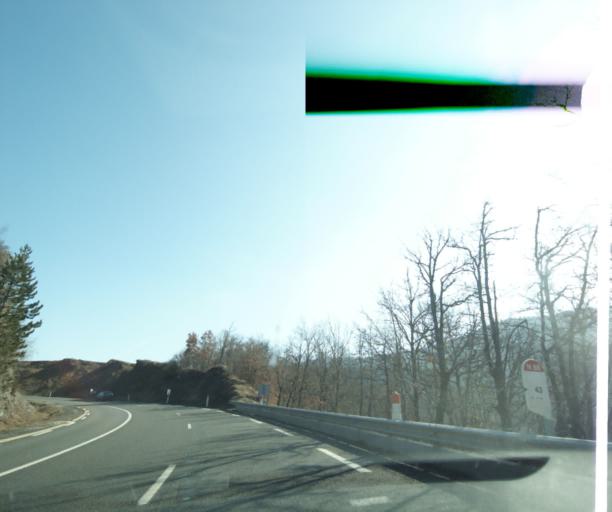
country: FR
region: Languedoc-Roussillon
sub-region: Departement de la Lozere
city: Mende
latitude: 44.5350
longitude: 3.5672
